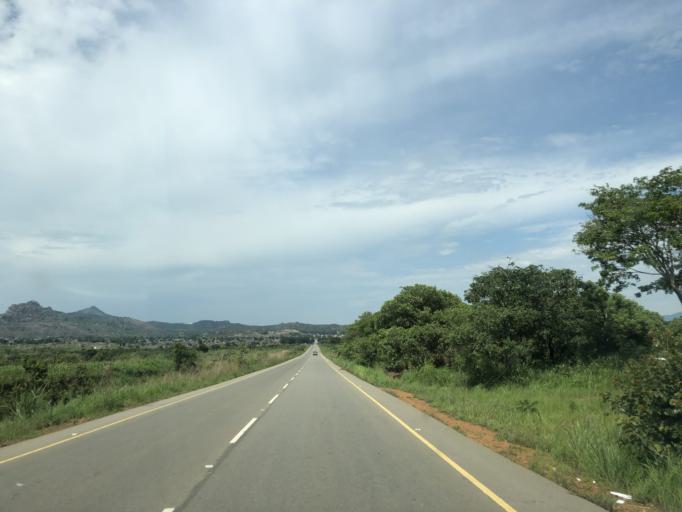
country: AO
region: Cuanza Sul
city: Quibala
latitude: -10.7342
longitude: 15.0084
